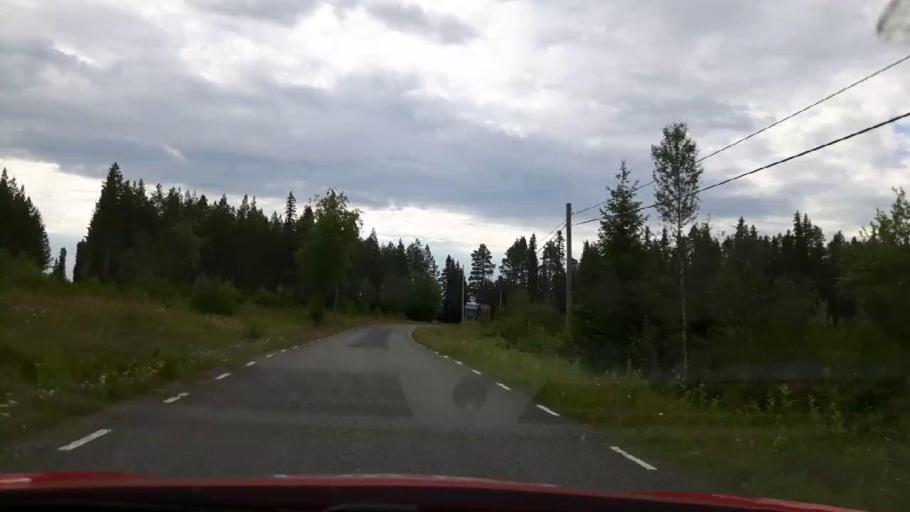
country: SE
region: Jaemtland
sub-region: OEstersunds Kommun
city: Lit
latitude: 63.3916
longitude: 15.0123
